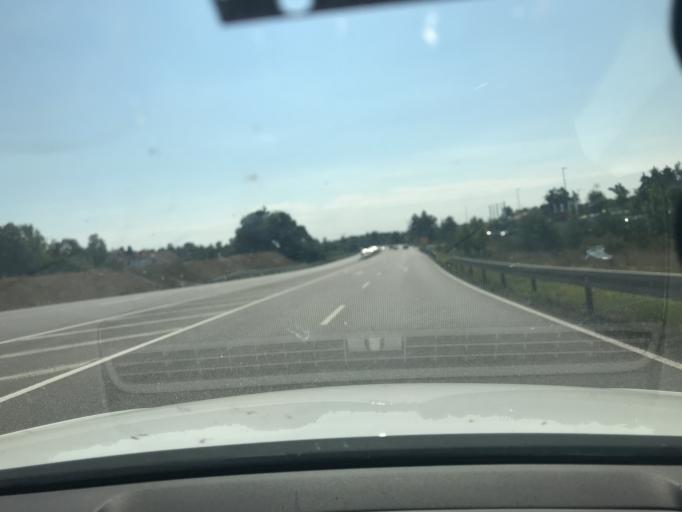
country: DE
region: Bavaria
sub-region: Upper Palatinate
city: Amberg
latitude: 49.4514
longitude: 11.8264
